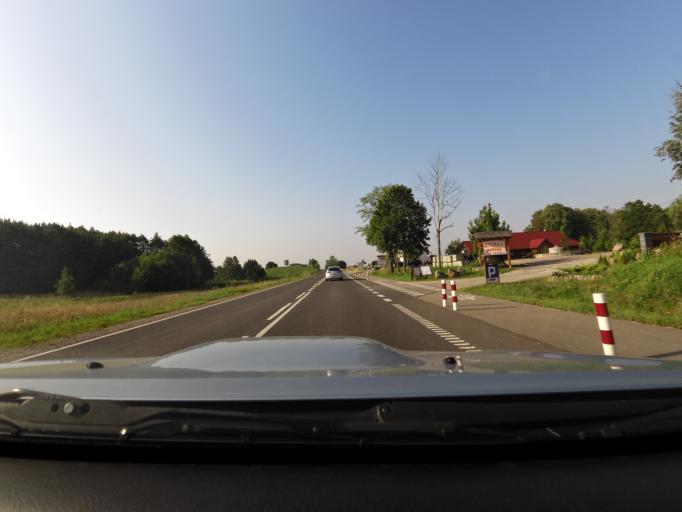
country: LT
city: Lazdijai
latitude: 54.1466
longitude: 23.4683
